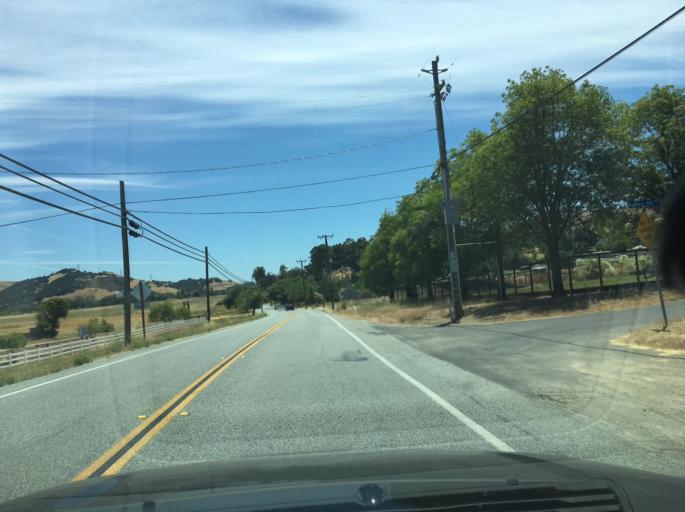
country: US
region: California
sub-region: Santa Clara County
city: Seven Trees
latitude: 37.1985
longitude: -121.8194
